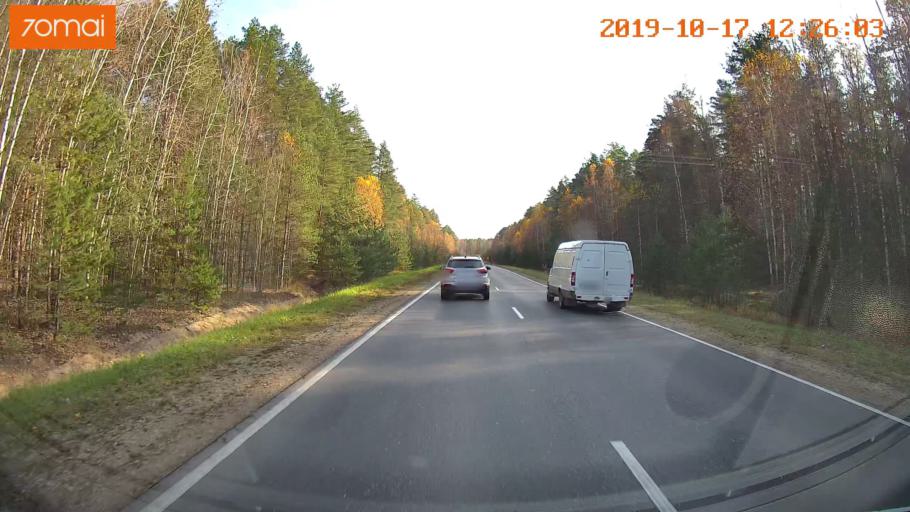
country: RU
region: Rjazan
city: Syntul
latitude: 55.0225
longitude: 41.2485
